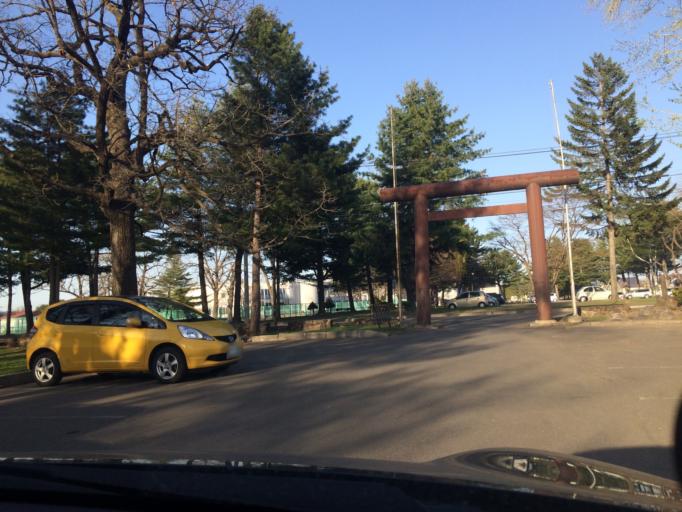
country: JP
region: Hokkaido
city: Obihiro
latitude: 42.9186
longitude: 143.0483
